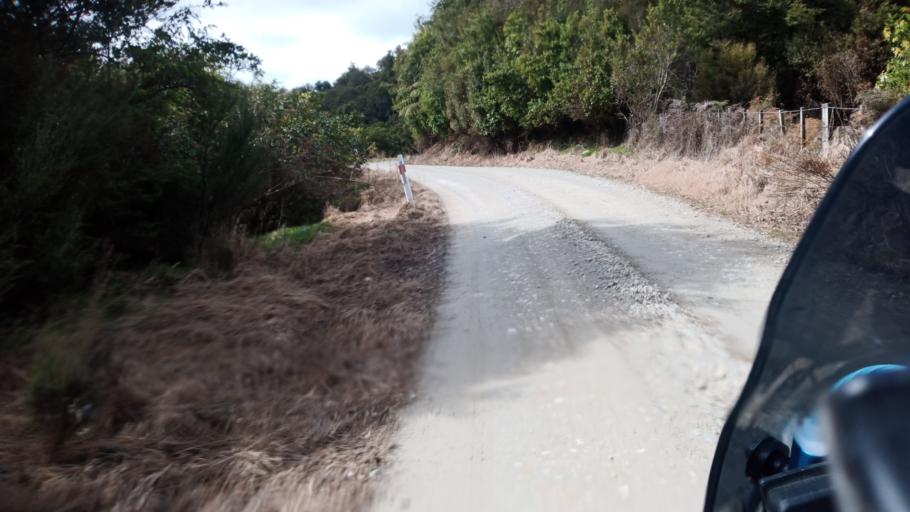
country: NZ
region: Gisborne
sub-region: Gisborne District
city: Gisborne
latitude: -38.8508
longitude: 177.7885
